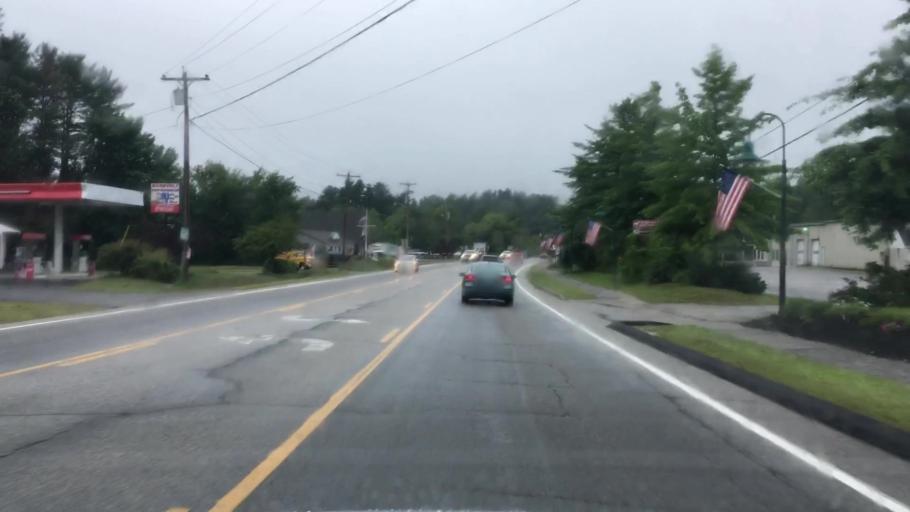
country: US
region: Maine
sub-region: Cumberland County
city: Raymond
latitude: 43.8868
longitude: -70.4646
